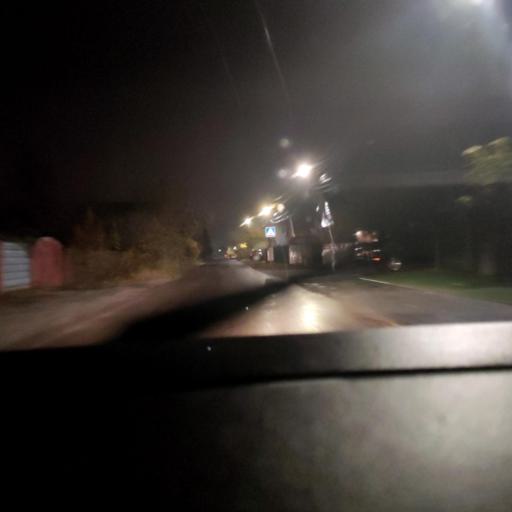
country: RU
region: Voronezj
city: Semiluki
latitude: 51.7064
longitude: 39.0289
